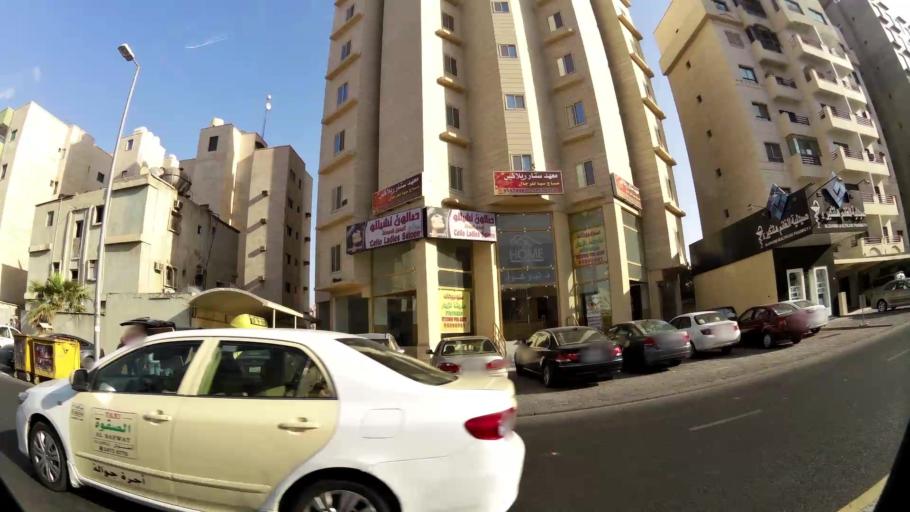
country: KW
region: Muhafazat Hawalli
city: As Salimiyah
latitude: 29.3348
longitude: 48.0850
